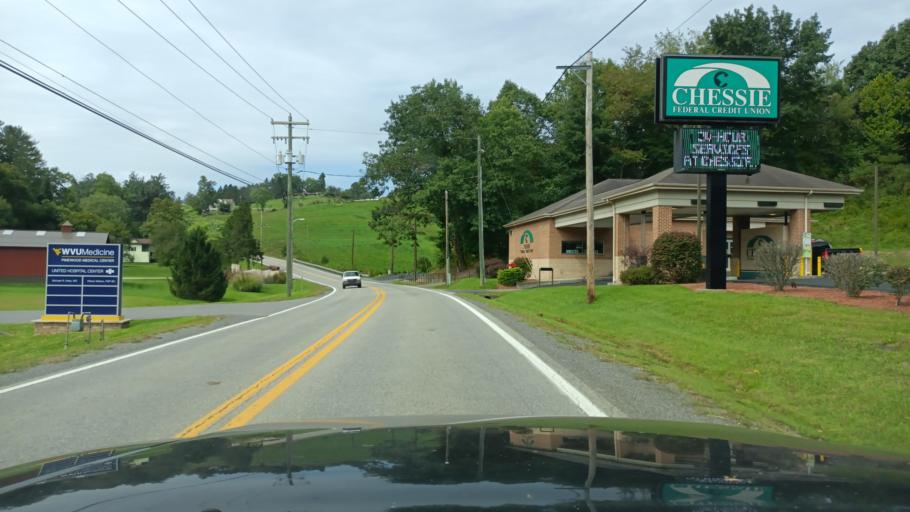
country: US
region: West Virginia
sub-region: Taylor County
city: Grafton
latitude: 39.3485
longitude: -80.0085
